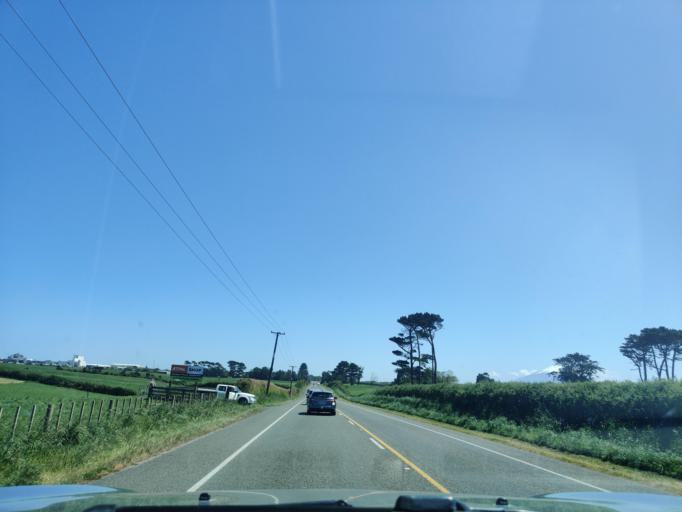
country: NZ
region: Taranaki
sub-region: South Taranaki District
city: Hawera
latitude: -39.6092
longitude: 174.3223
